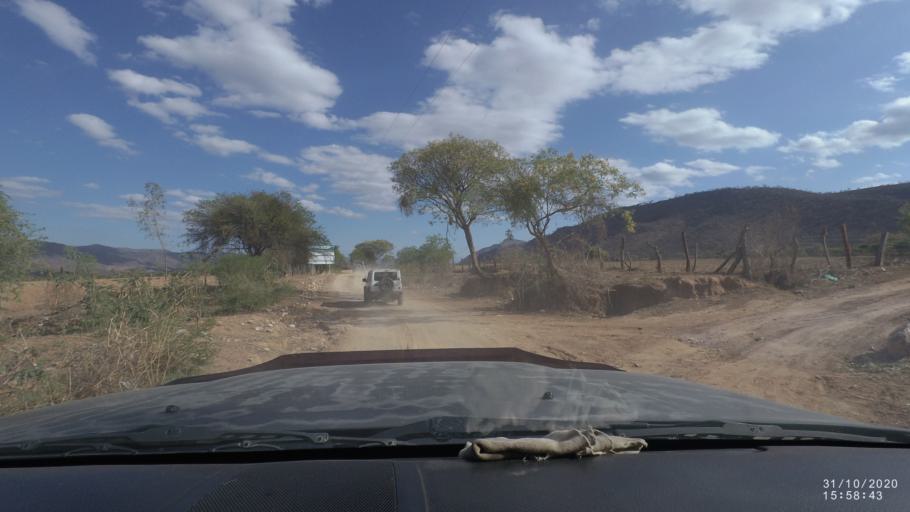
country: BO
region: Chuquisaca
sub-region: Provincia Zudanez
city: Mojocoya
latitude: -18.3265
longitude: -64.6710
